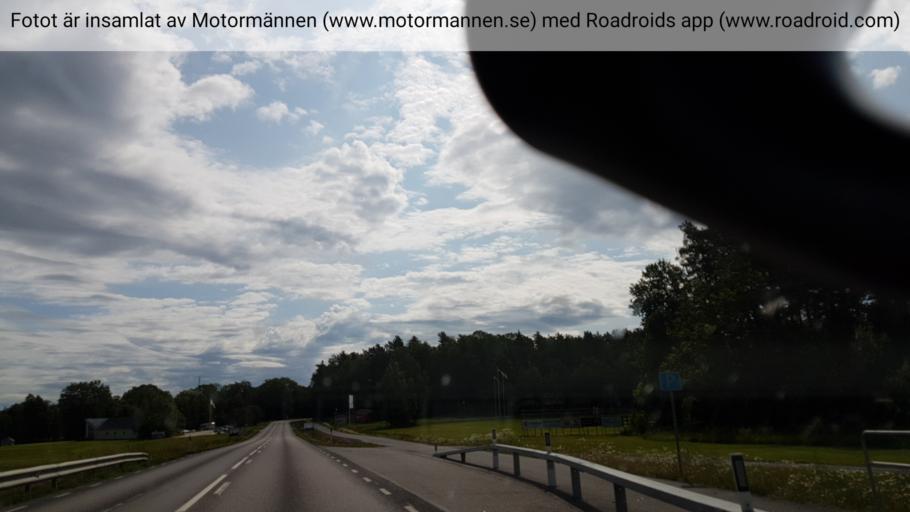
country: SE
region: Vaestra Goetaland
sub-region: Grastorps Kommun
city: Graestorp
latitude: 58.3346
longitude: 12.6613
